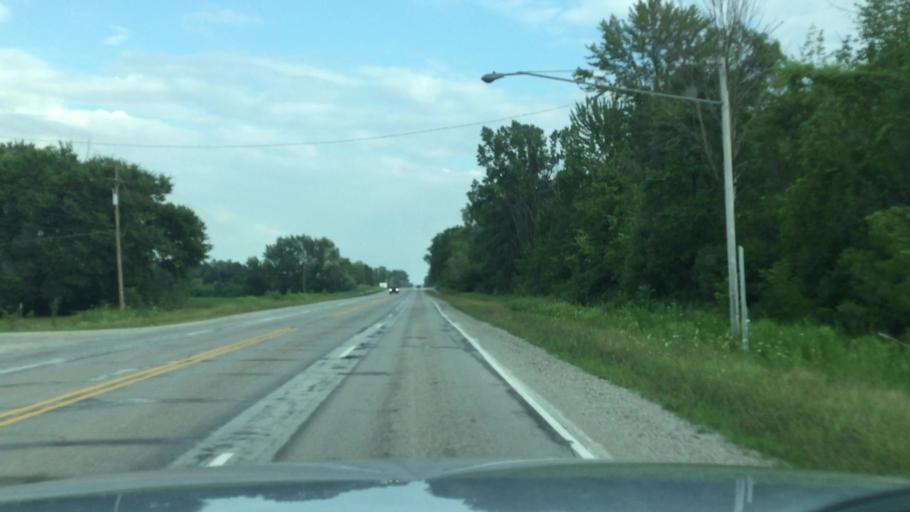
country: US
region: Michigan
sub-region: Saginaw County
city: Birch Run
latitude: 43.2720
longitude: -83.7859
